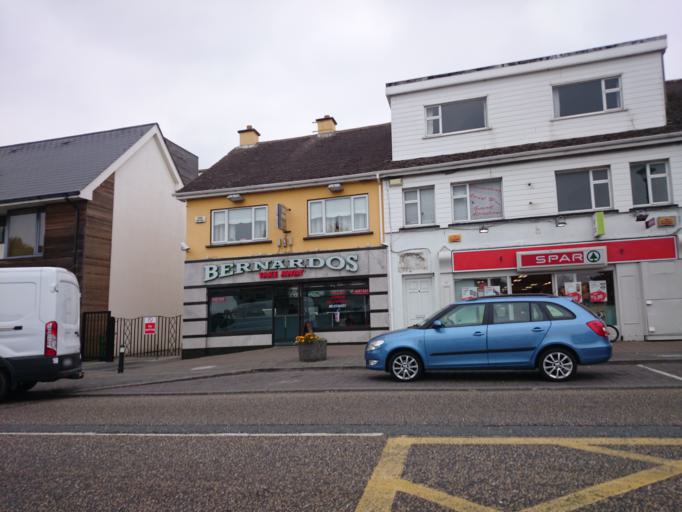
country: IE
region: Leinster
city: Shankill
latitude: 53.2308
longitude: -6.1240
